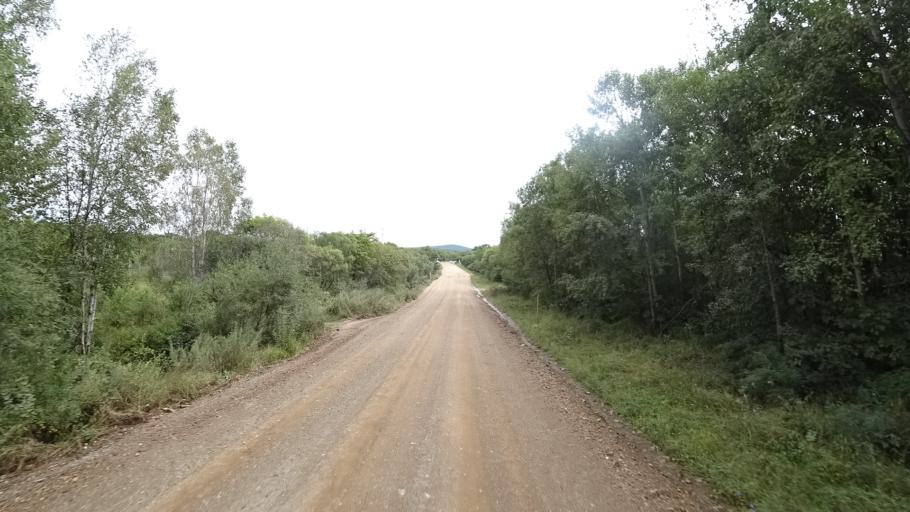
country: RU
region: Primorskiy
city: Lyalichi
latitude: 44.0836
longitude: 132.4453
